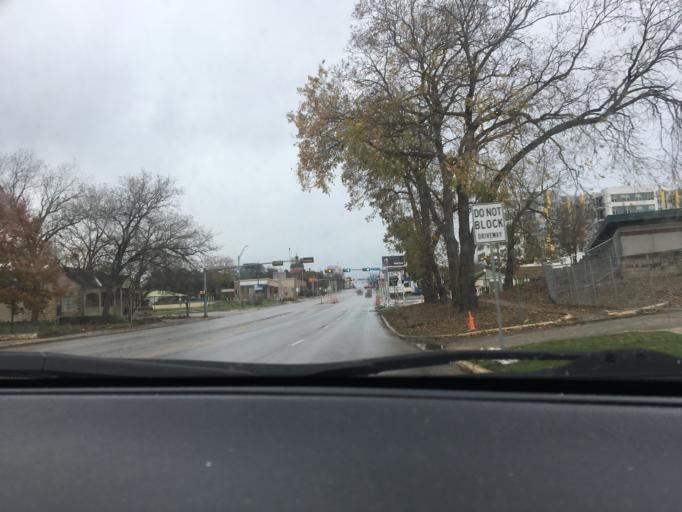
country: US
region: Texas
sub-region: Hays County
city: San Marcos
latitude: 29.8838
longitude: -97.9367
